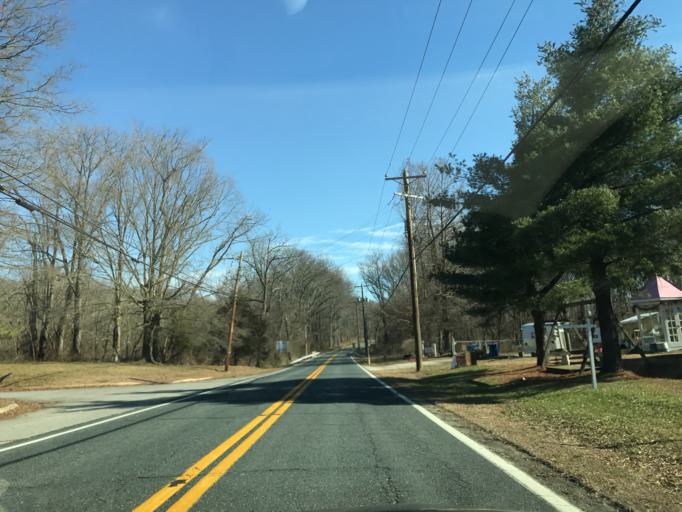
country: US
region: Maryland
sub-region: Queen Anne's County
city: Grasonville
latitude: 38.9849
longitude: -76.1478
